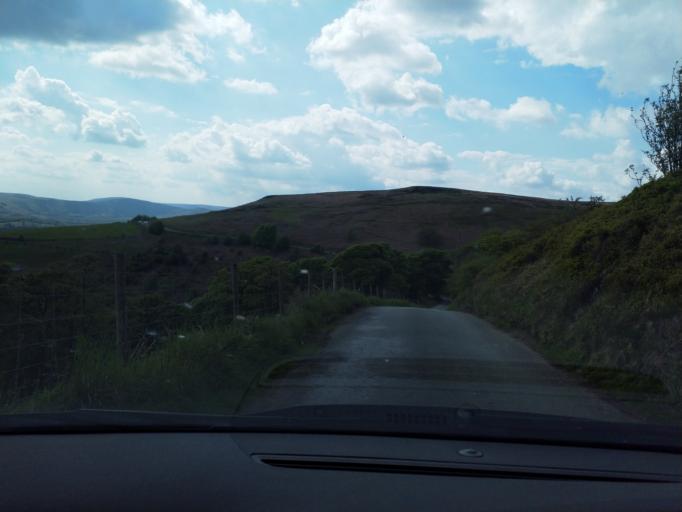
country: GB
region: England
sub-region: Derbyshire
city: Hathersage
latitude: 53.3521
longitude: -1.6691
